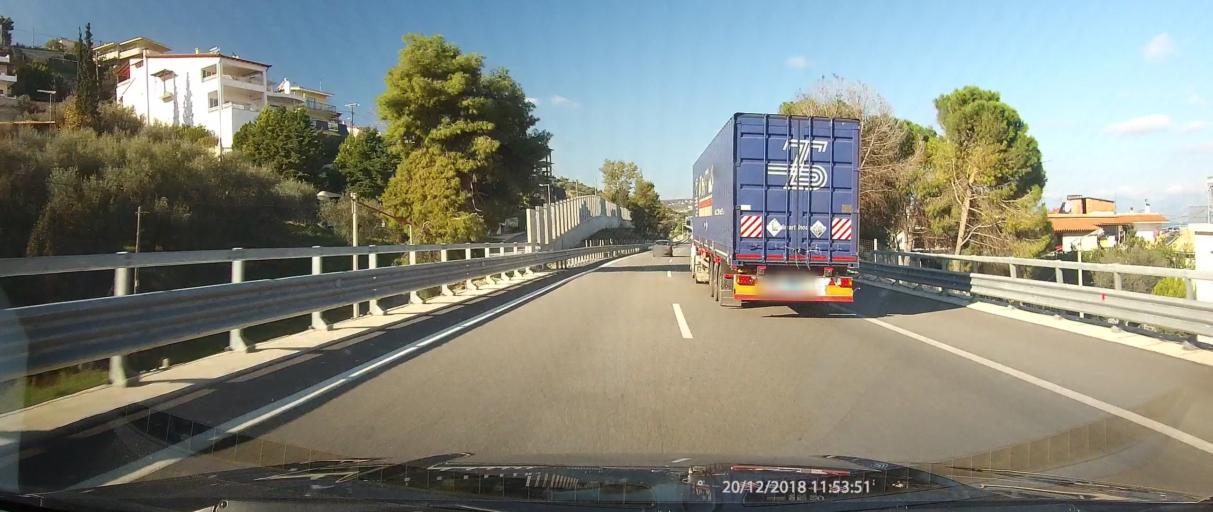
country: GR
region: West Greece
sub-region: Nomos Achaias
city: Aiyira
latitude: 38.1474
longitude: 22.3542
